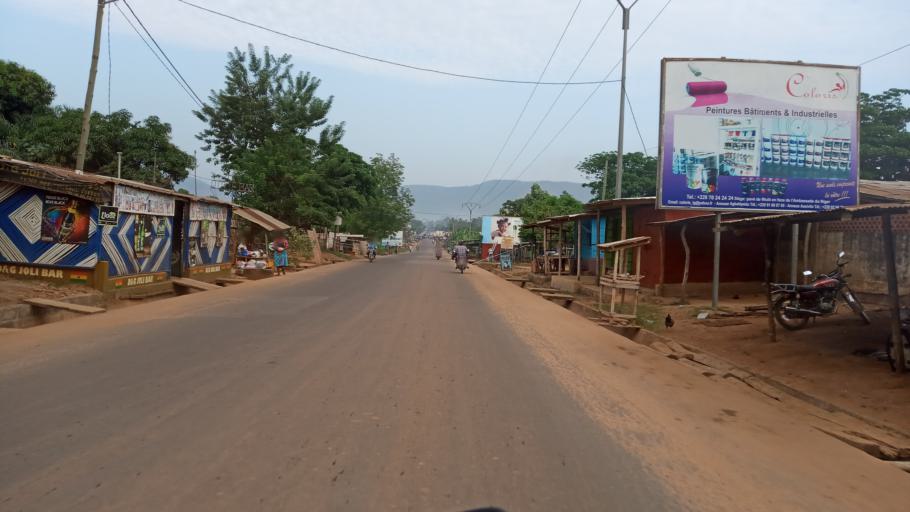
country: TG
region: Plateaux
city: Kpalime
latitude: 6.8965
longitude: 0.6375
